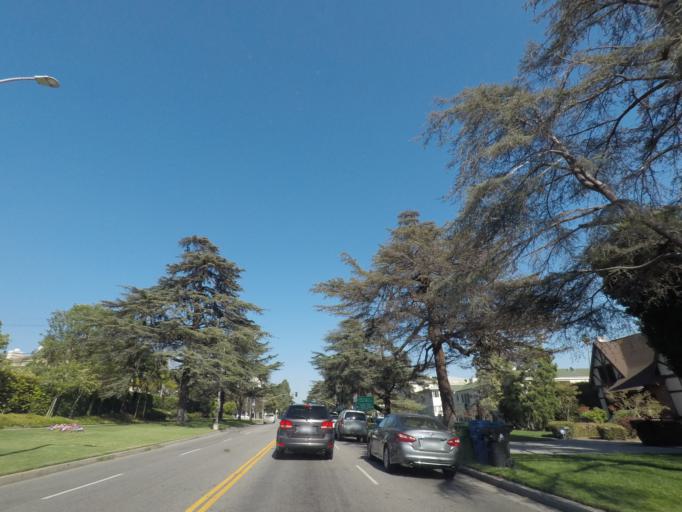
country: US
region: California
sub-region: Los Angeles County
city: Silver Lake
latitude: 34.1108
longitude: -118.2932
